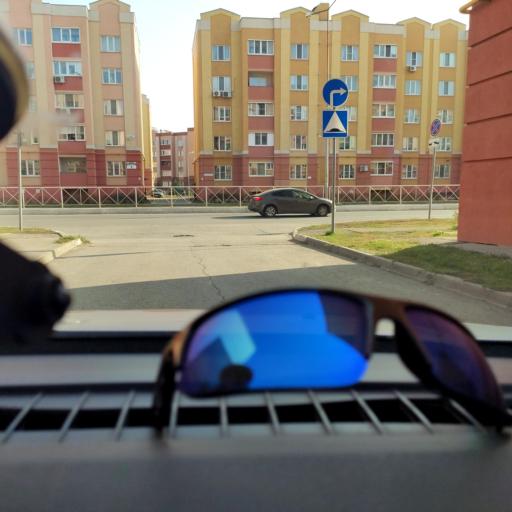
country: RU
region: Samara
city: Samara
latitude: 53.1177
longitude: 50.1588
